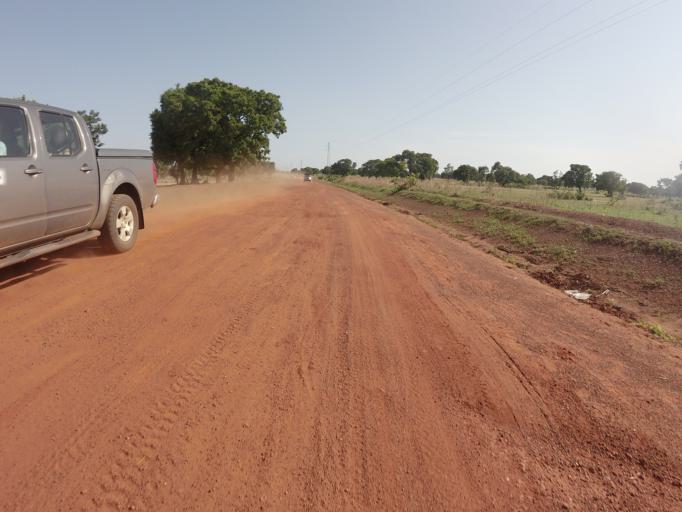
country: GH
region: Upper East
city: Bawku
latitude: 10.7776
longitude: -0.1924
